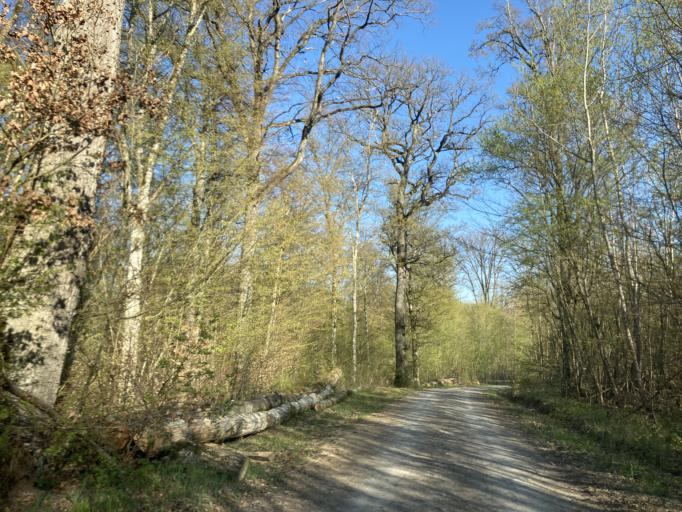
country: DE
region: Baden-Wuerttemberg
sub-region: Regierungsbezirk Stuttgart
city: Hildrizhausen
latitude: 48.5587
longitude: 8.9393
